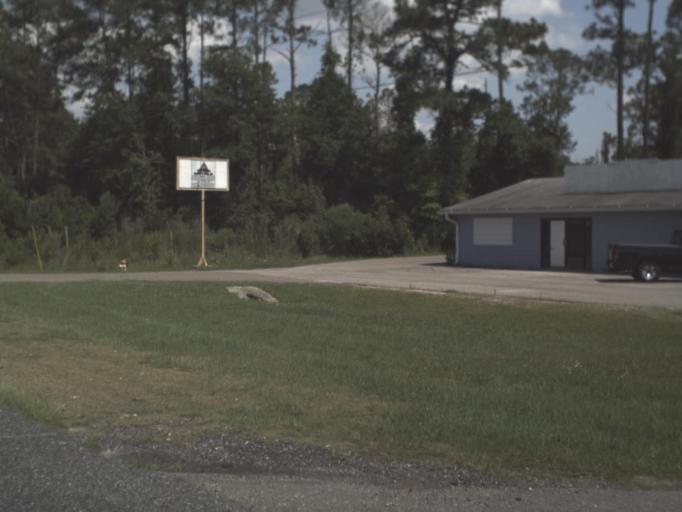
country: US
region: Florida
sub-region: Alachua County
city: Hawthorne
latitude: 29.5973
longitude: -82.1083
